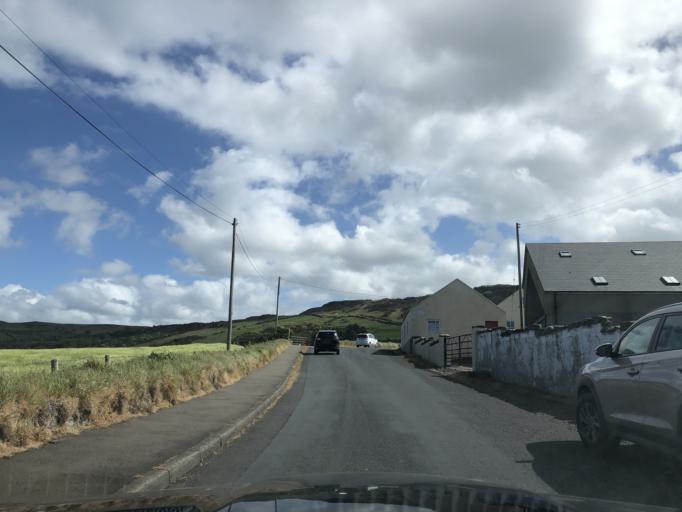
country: GB
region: Northern Ireland
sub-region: Moyle District
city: Ballycastle
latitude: 55.2389
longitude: -6.3659
